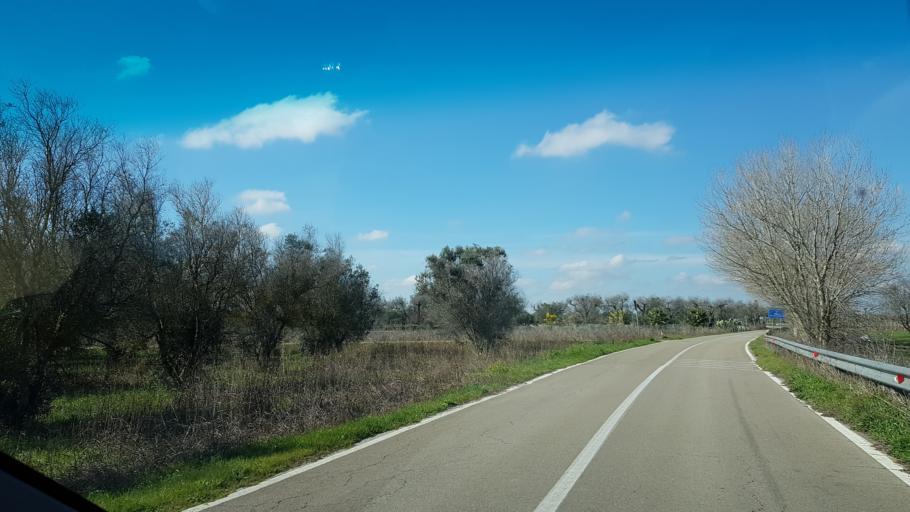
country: IT
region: Apulia
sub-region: Provincia di Brindisi
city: Cellino San Marco
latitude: 40.4395
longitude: 17.9920
